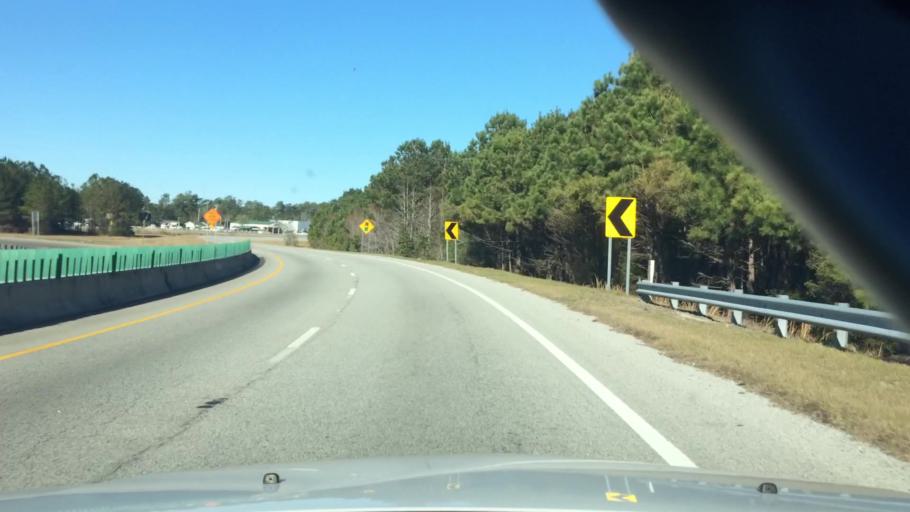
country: US
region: South Carolina
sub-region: Horry County
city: North Myrtle Beach
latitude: 33.8782
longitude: -78.6829
